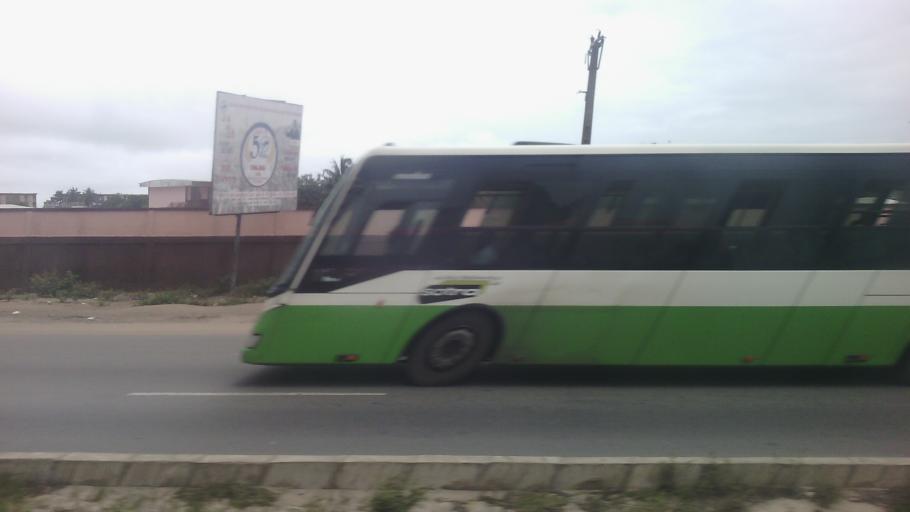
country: CI
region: Lagunes
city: Abidjan
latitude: 5.2553
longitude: -3.9569
